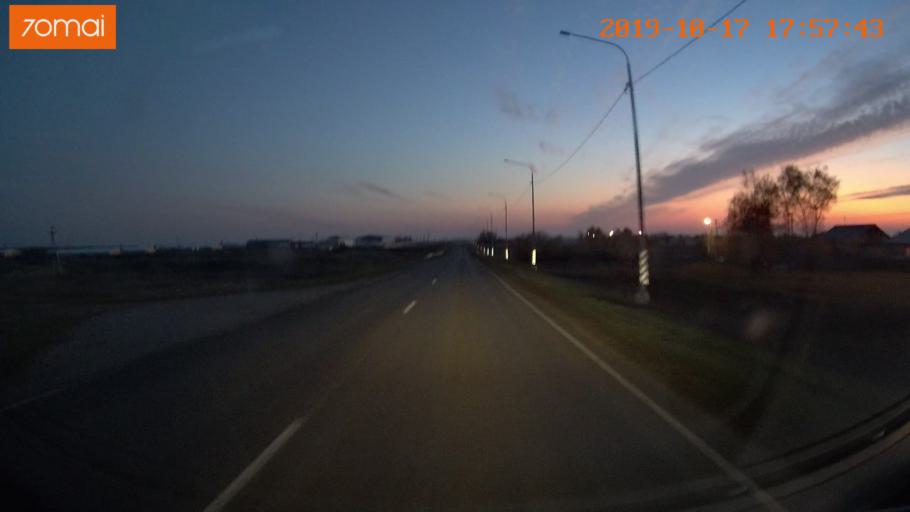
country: RU
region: Tula
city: Kurkino
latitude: 53.5633
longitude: 38.6332
